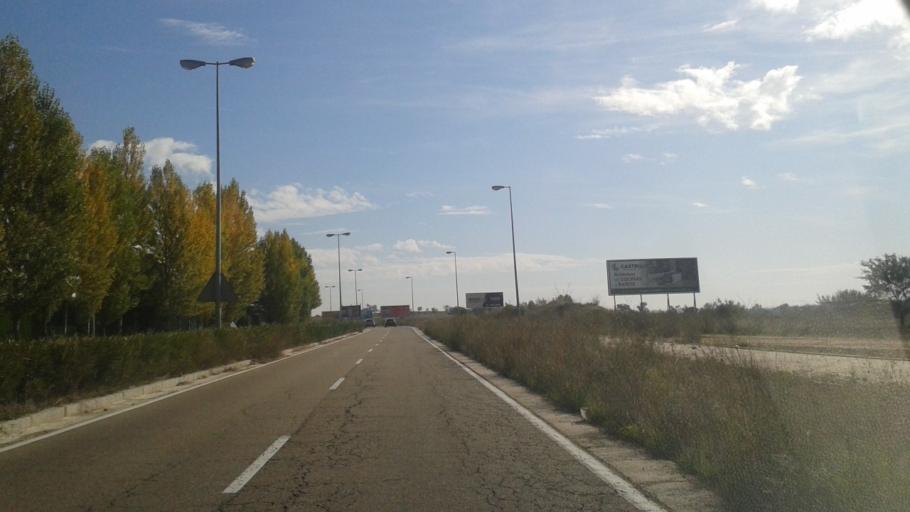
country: ES
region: Castille and Leon
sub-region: Provincia de Valladolid
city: Zaratan
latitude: 41.6330
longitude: -4.7723
